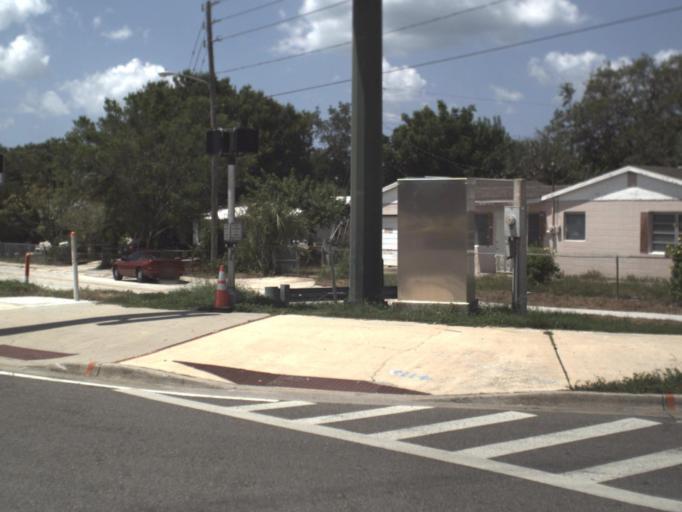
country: US
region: Florida
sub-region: Pinellas County
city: Ridgecrest
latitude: 27.8948
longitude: -82.8036
